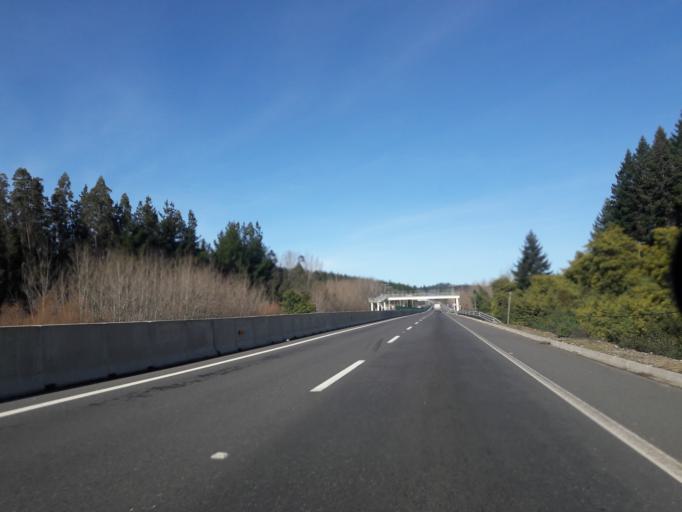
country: CL
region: Biobio
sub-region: Provincia de Concepcion
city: Chiguayante
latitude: -36.9146
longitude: -72.7763
